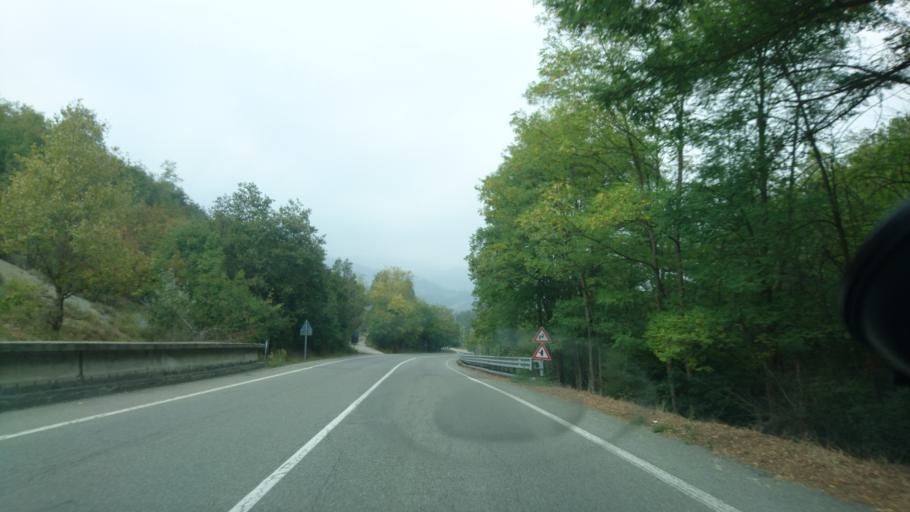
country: IT
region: Piedmont
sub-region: Provincia di Asti
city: Mombaldone
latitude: 44.5768
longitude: 8.3497
